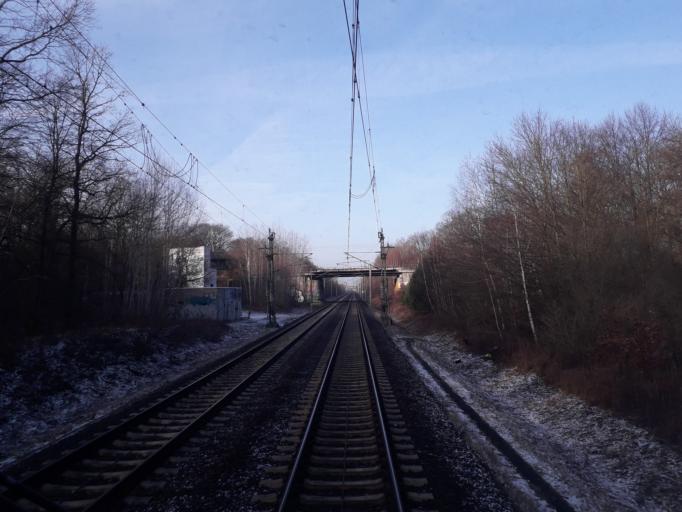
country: DE
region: Brandenburg
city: Brieselang
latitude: 52.5775
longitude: 13.0209
